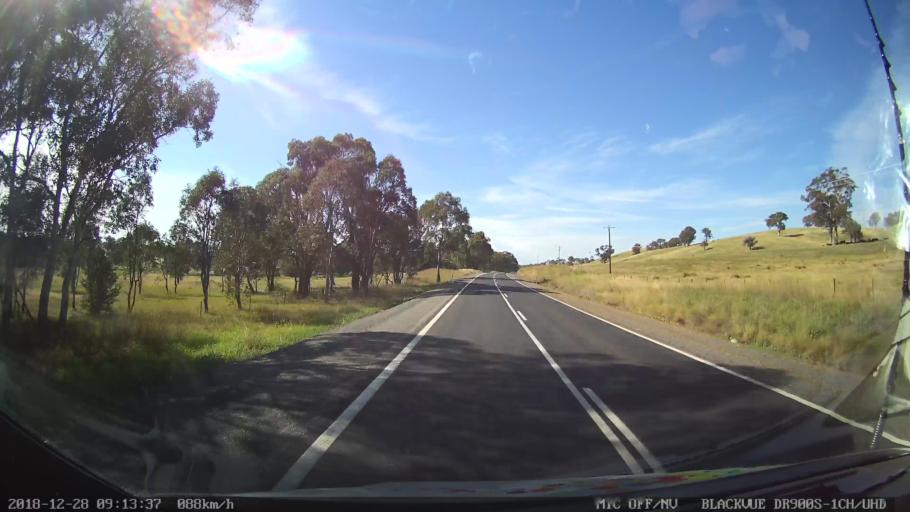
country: AU
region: New South Wales
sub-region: Upper Lachlan Shire
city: Crookwell
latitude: -34.2713
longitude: 149.3442
